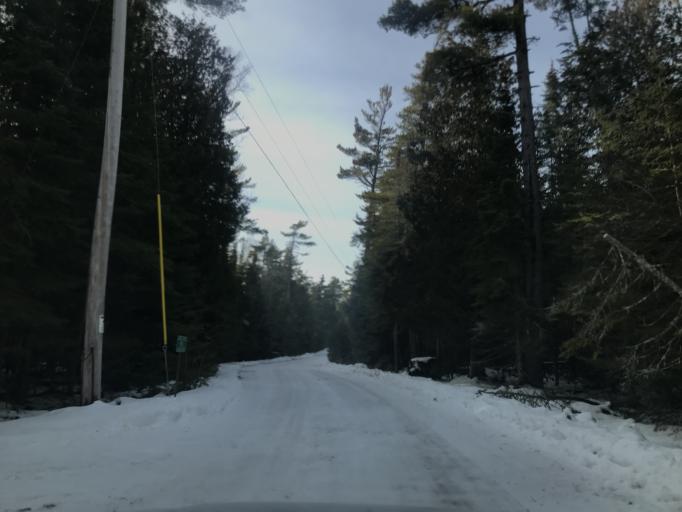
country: US
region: Wisconsin
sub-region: Door County
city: Sturgeon Bay
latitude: 45.1419
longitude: -87.0392
